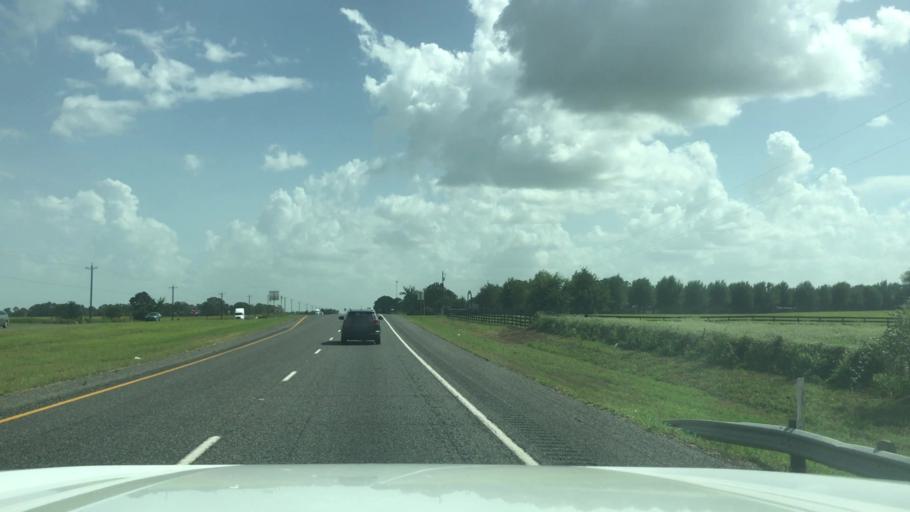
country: US
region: Texas
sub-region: Waller County
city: Hempstead
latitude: 30.1475
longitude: -96.0703
